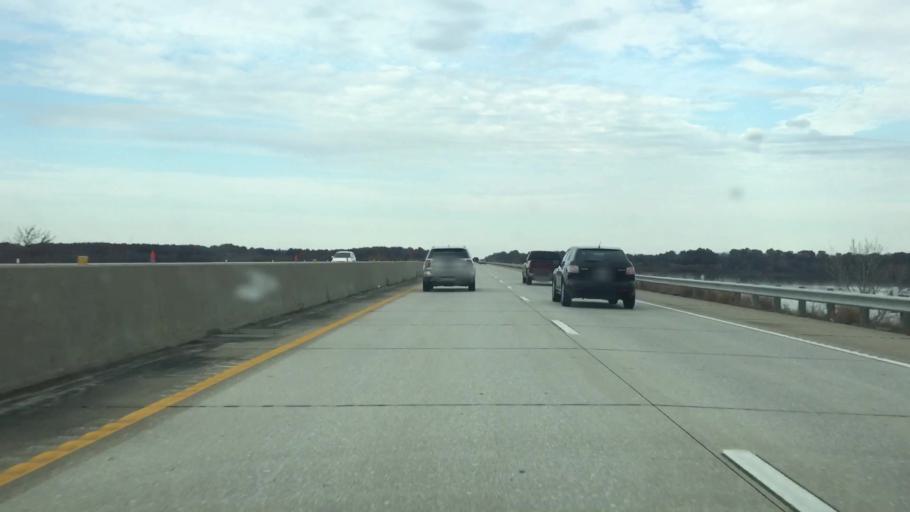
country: US
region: Missouri
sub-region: Henry County
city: Clinton
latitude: 38.2786
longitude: -93.7597
